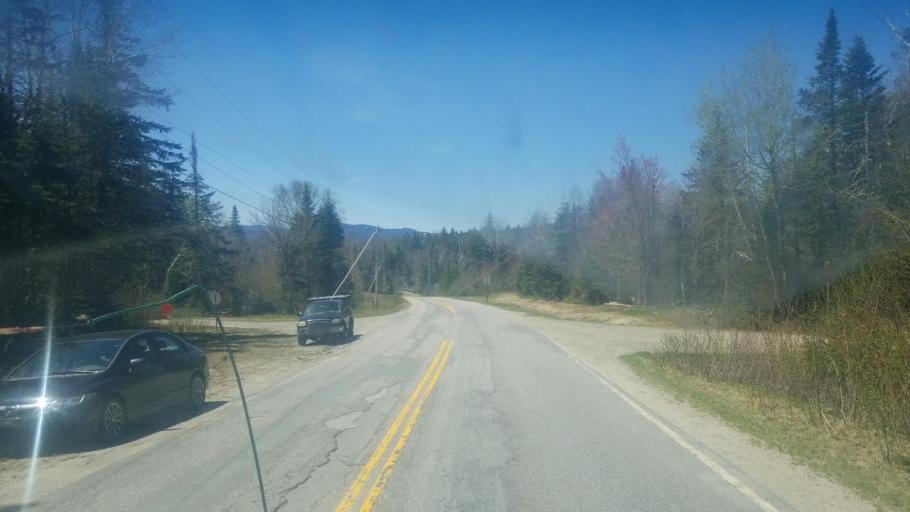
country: US
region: New Hampshire
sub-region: Coos County
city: Jefferson
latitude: 44.2638
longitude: -71.3819
